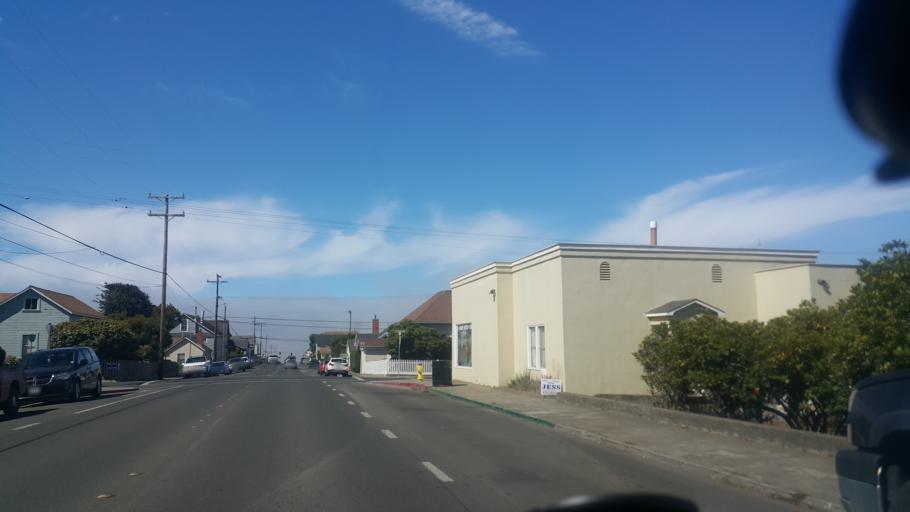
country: US
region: California
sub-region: Mendocino County
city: Fort Bragg
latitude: 39.4417
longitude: -123.8016
